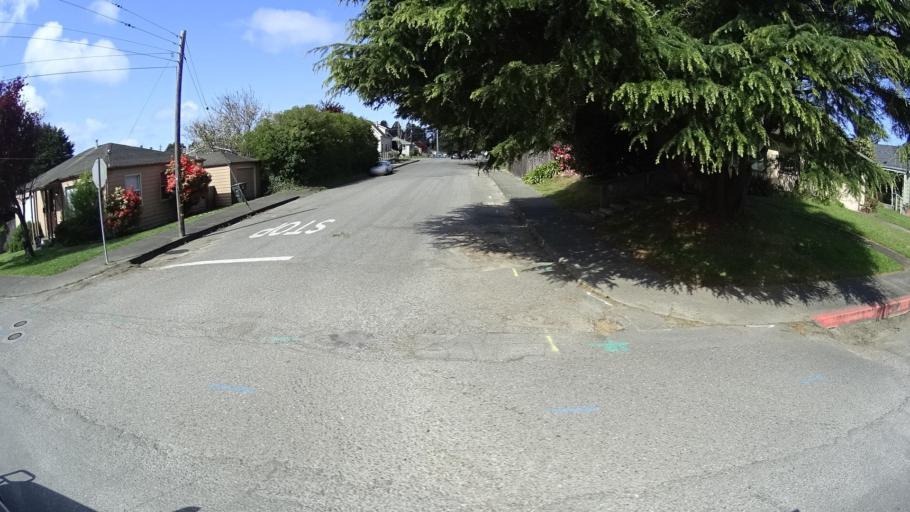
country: US
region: California
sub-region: Humboldt County
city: Cutten
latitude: 40.7762
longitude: -124.1614
